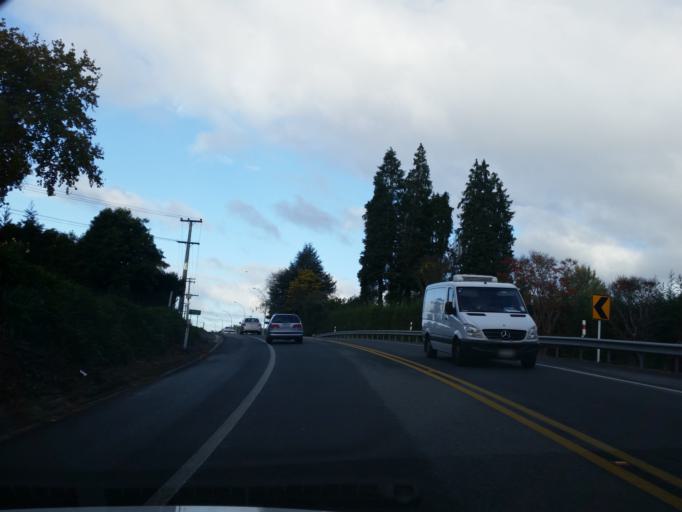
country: NZ
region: Bay of Plenty
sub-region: Tauranga City
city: Tauranga
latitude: -37.7000
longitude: 176.0786
